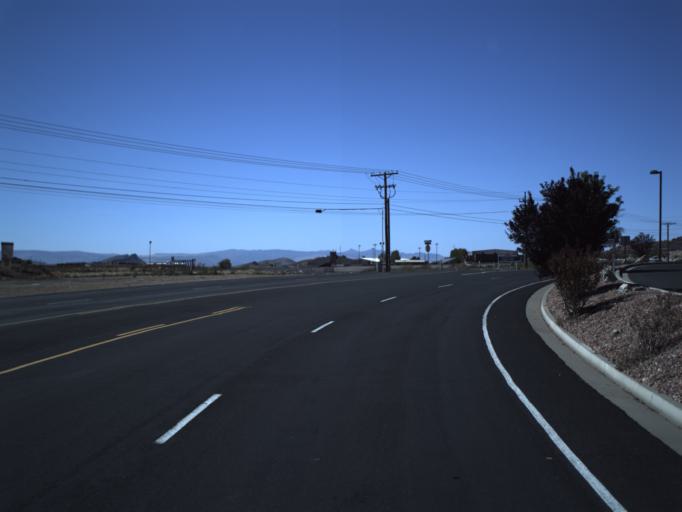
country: US
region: Utah
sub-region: Washington County
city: Washington
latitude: 37.1669
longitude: -113.4084
